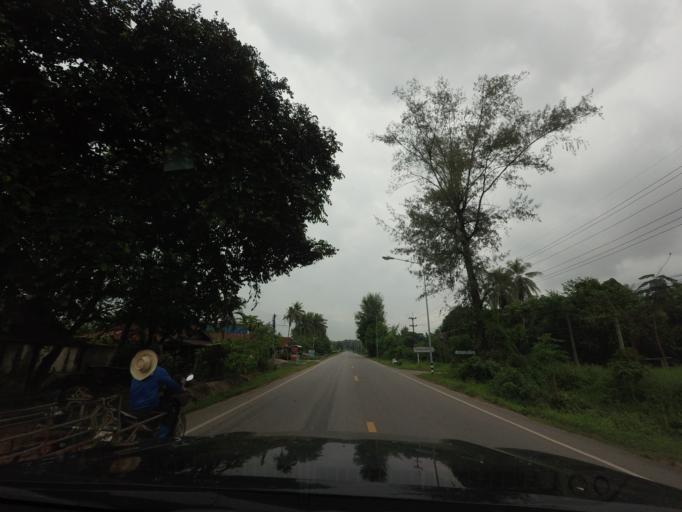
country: TH
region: Nong Khai
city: Si Chiang Mai
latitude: 17.9596
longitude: 102.5467
